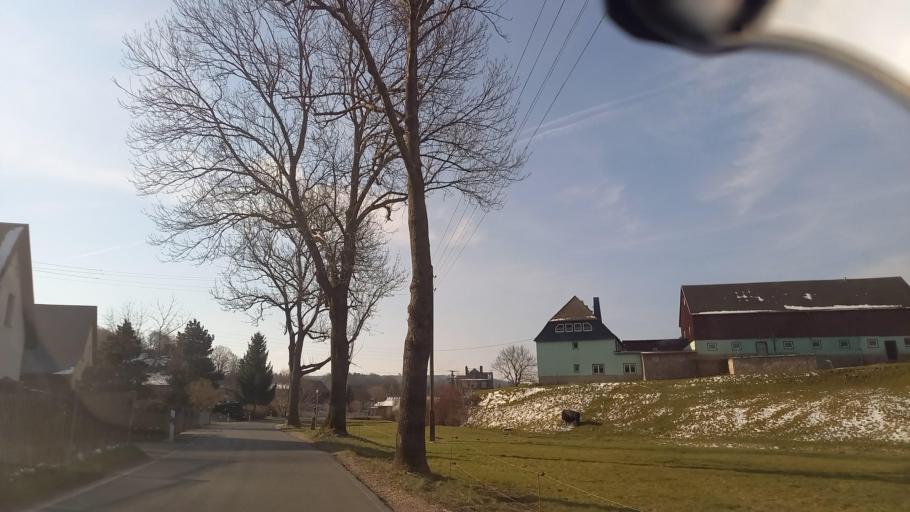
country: DE
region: Saxony
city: Kirchberg
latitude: 50.5802
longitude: 12.4923
